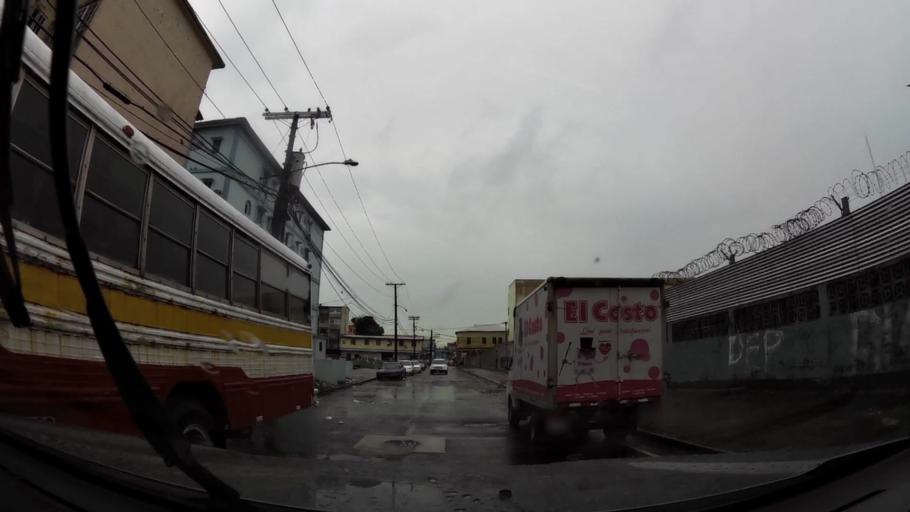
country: PA
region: Colon
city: Colon
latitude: 9.3658
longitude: -79.9023
